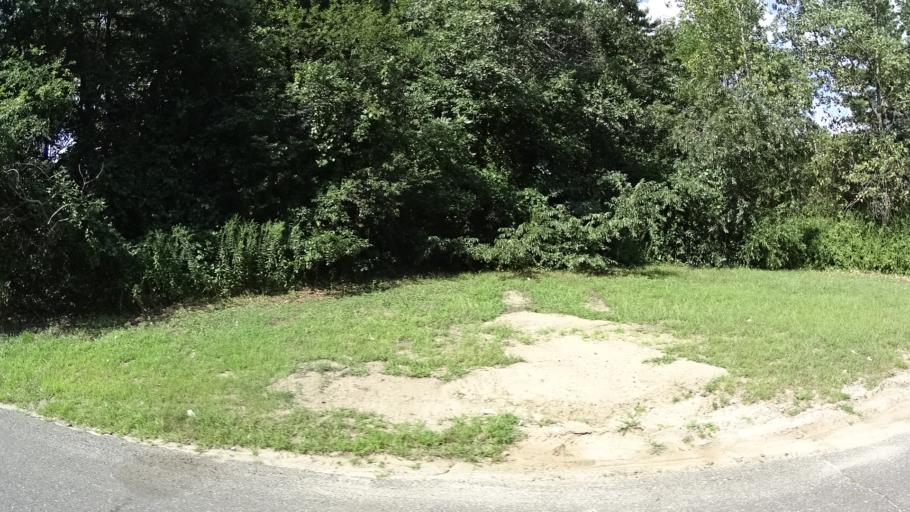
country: US
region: New Jersey
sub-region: Monmouth County
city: Eatontown
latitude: 40.2824
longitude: -74.0778
